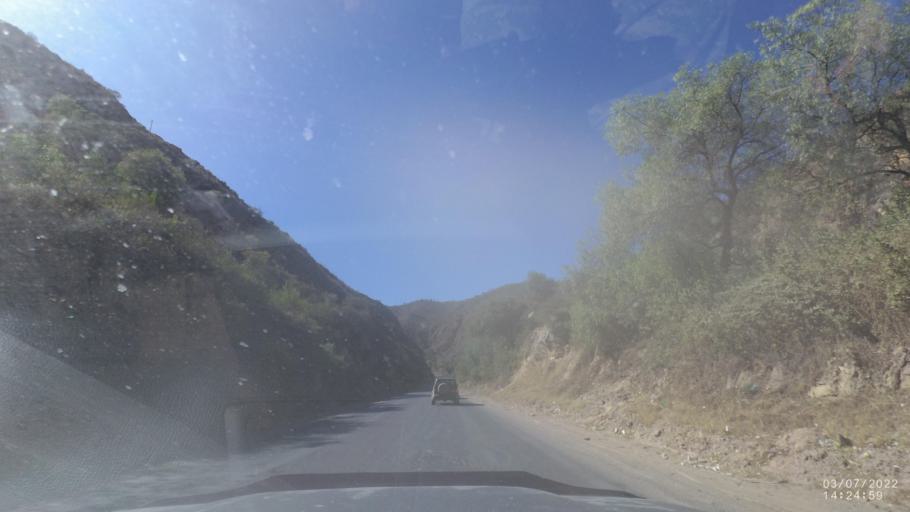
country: BO
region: Cochabamba
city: Sipe Sipe
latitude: -17.5245
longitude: -66.3319
